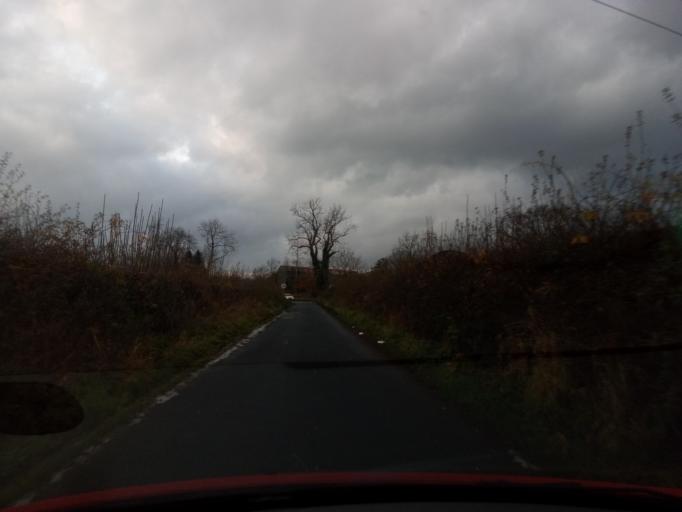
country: GB
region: Scotland
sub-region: The Scottish Borders
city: Newtown St Boswells
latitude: 55.5865
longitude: -2.6760
